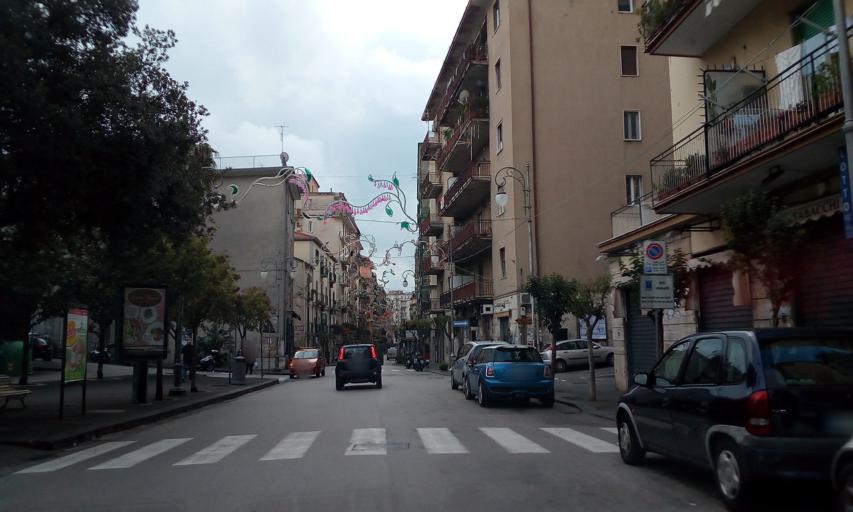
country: IT
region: Campania
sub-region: Provincia di Salerno
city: Capezzano Inferiore
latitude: 40.6846
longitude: 14.7707
